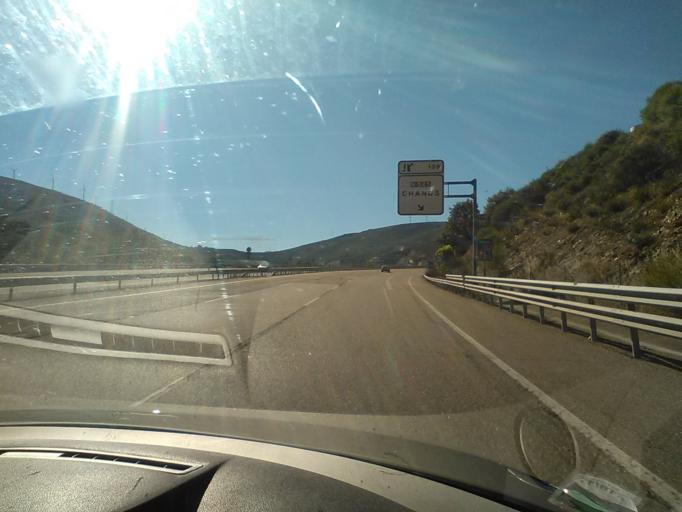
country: ES
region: Castille and Leon
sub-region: Provincia de Zamora
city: Lubian
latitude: 42.0343
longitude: -6.9305
